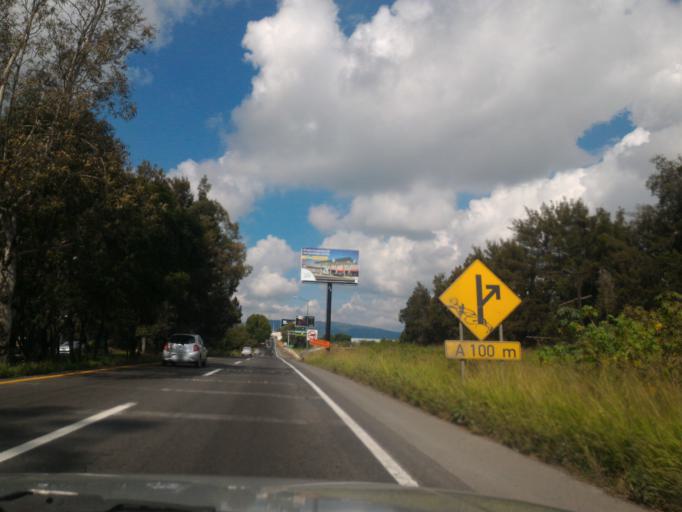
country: MX
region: Jalisco
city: Nuevo Mexico
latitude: 20.7164
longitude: -103.4758
